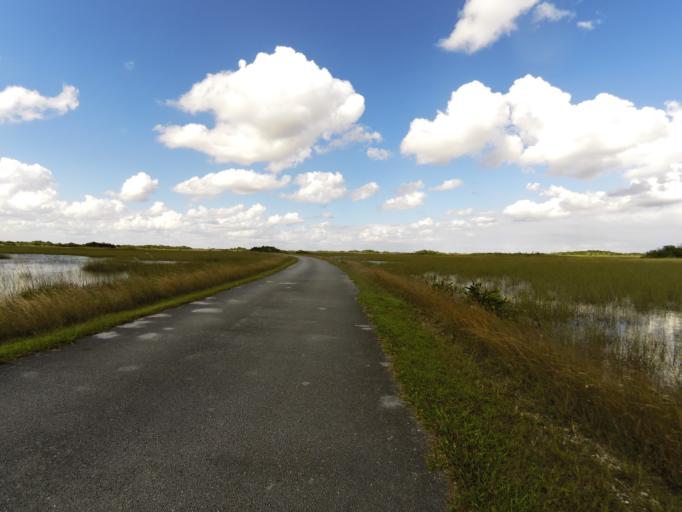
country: US
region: Florida
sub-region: Miami-Dade County
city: The Hammocks
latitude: 25.7038
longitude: -80.7606
